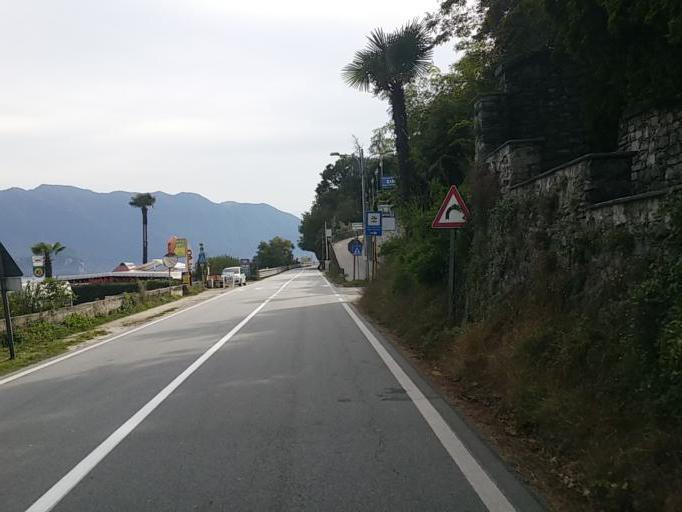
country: IT
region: Piedmont
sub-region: Provincia Verbano-Cusio-Ossola
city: Gonte
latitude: 46.0000
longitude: 8.6564
